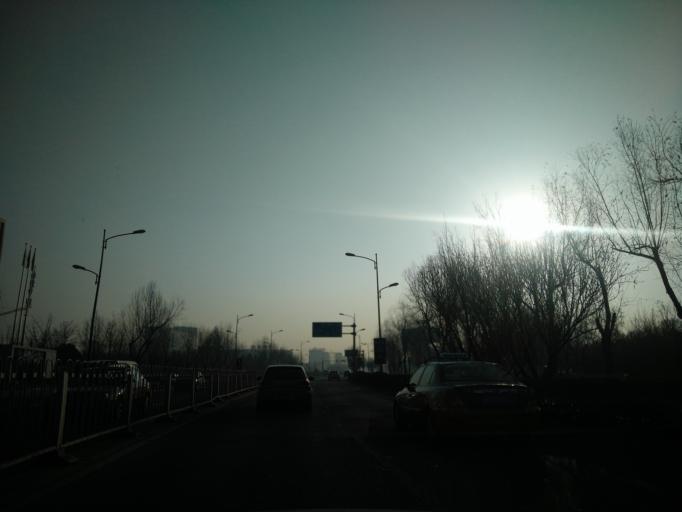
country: CN
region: Beijing
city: Jiugong
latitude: 39.7741
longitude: 116.5082
